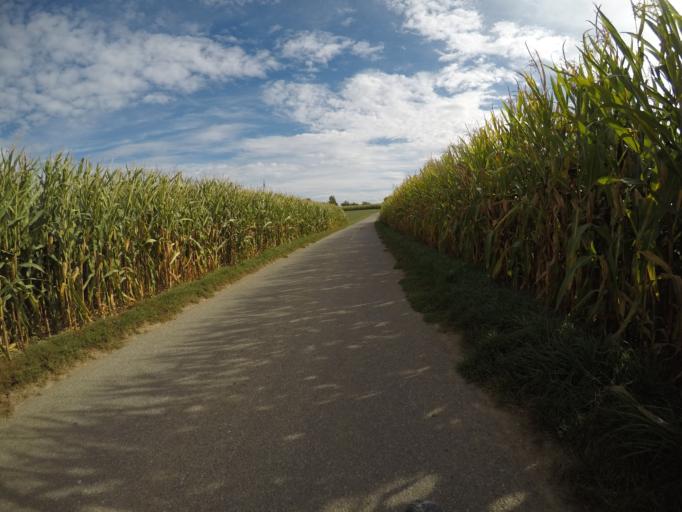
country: DE
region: Baden-Wuerttemberg
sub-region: Regierungsbezirk Stuttgart
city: Leonberg
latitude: 48.8302
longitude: 9.0035
